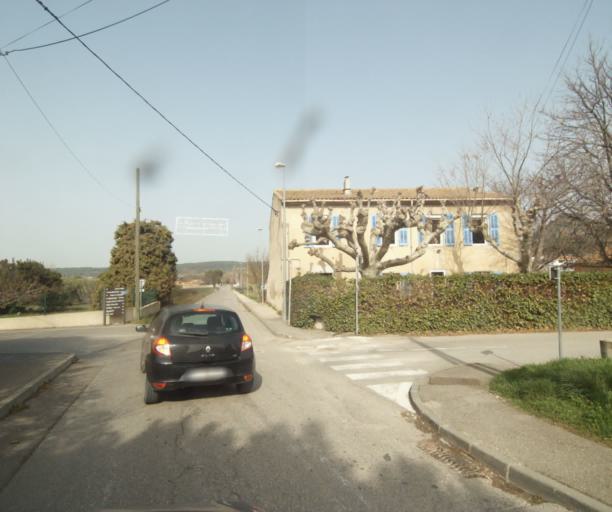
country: FR
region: Provence-Alpes-Cote d'Azur
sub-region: Departement des Bouches-du-Rhone
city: Simiane-Collongue
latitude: 43.4310
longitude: 5.4369
